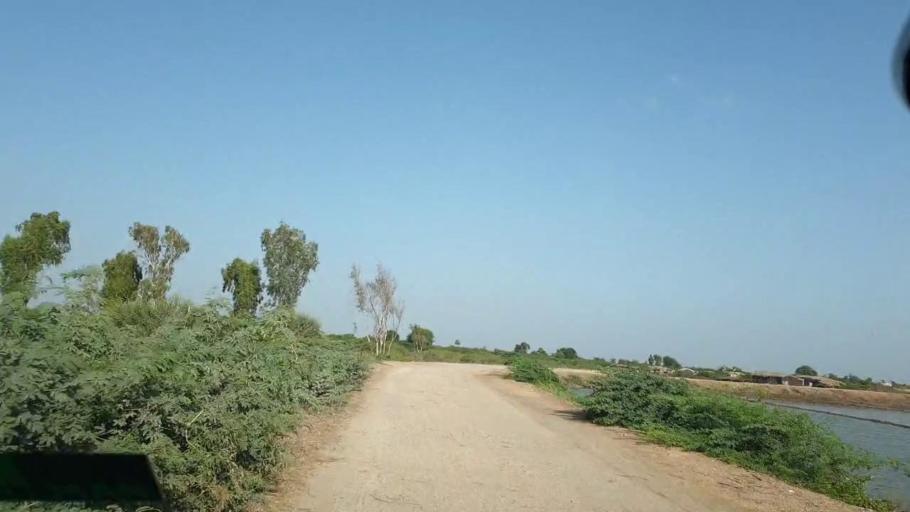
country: PK
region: Sindh
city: Naukot
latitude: 24.7408
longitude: 69.2052
